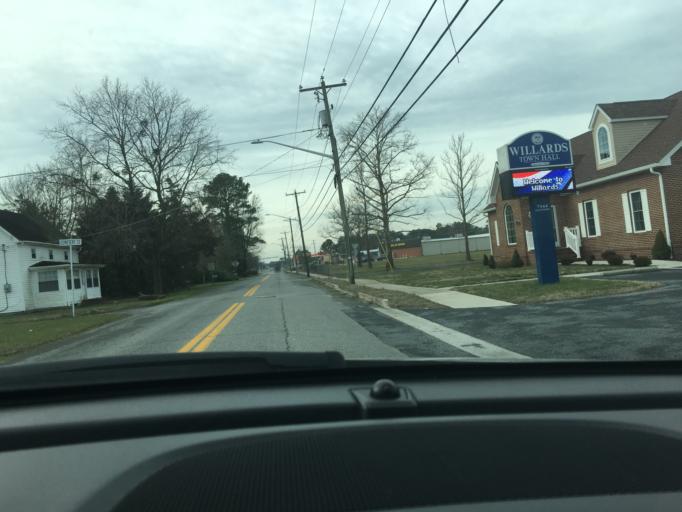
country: US
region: Maryland
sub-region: Wicomico County
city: Pittsville
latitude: 38.3912
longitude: -75.3509
